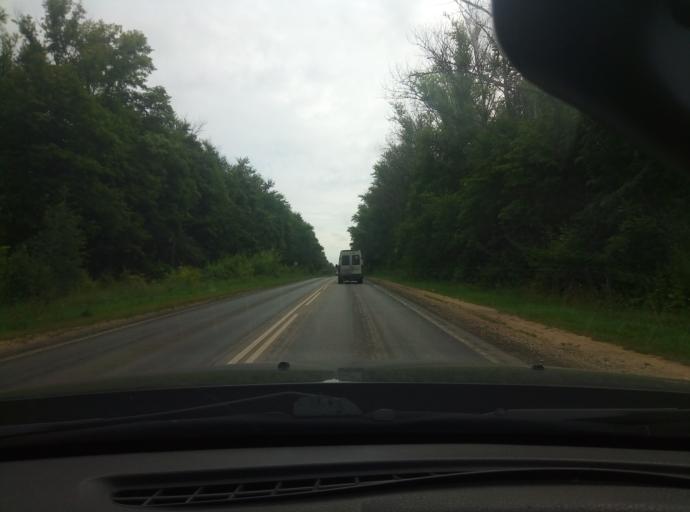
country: RU
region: Tula
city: Donskoy
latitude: 53.9694
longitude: 38.3918
